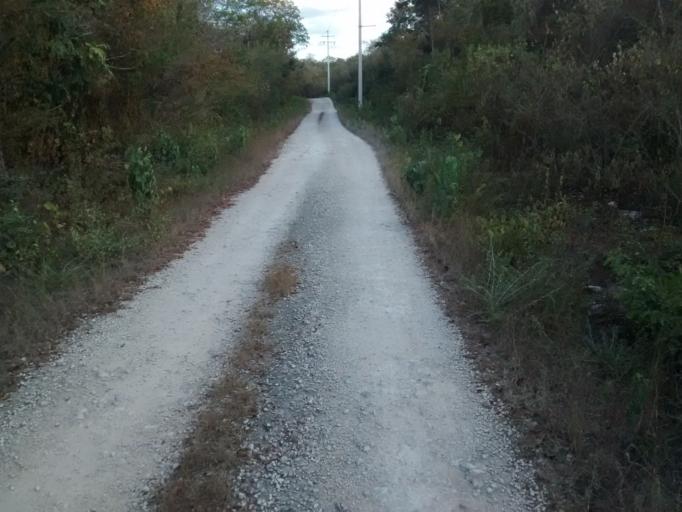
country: MX
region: Yucatan
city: Chichimila
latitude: 20.4480
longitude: -88.2007
